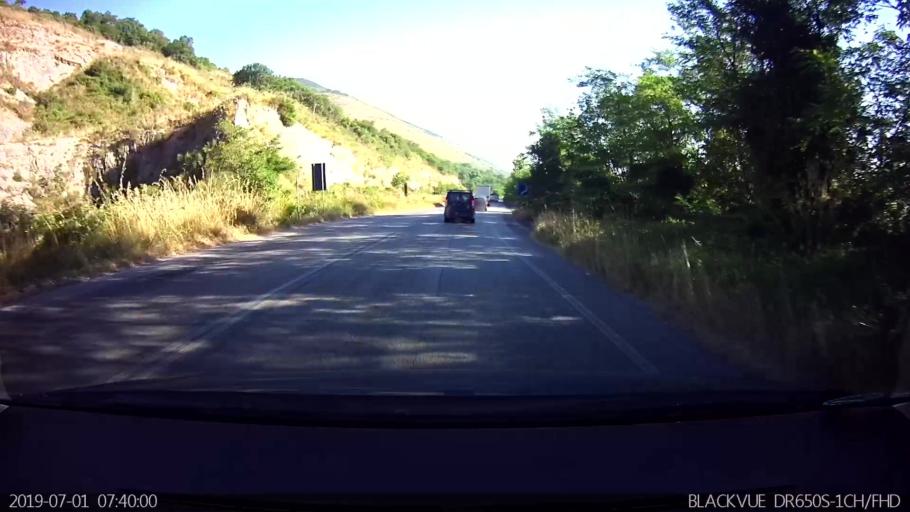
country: IT
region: Latium
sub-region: Provincia di Frosinone
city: Giuliano di Roma
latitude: 41.5541
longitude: 13.2667
